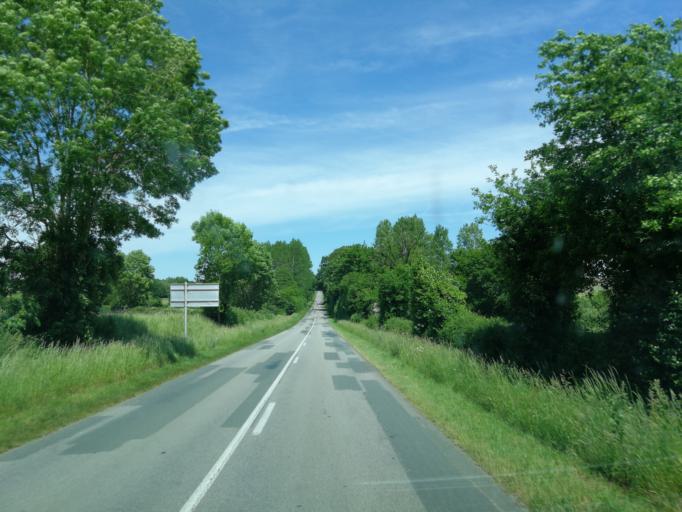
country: FR
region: Poitou-Charentes
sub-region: Departement des Deux-Sevres
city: Courlay
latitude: 46.7934
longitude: -0.5998
